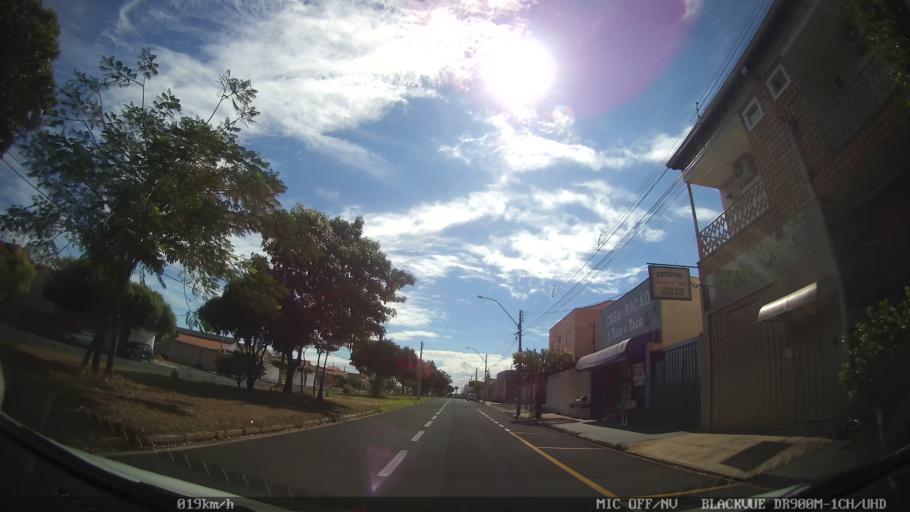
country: BR
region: Sao Paulo
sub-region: Bady Bassitt
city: Bady Bassitt
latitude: -20.8182
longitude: -49.4955
